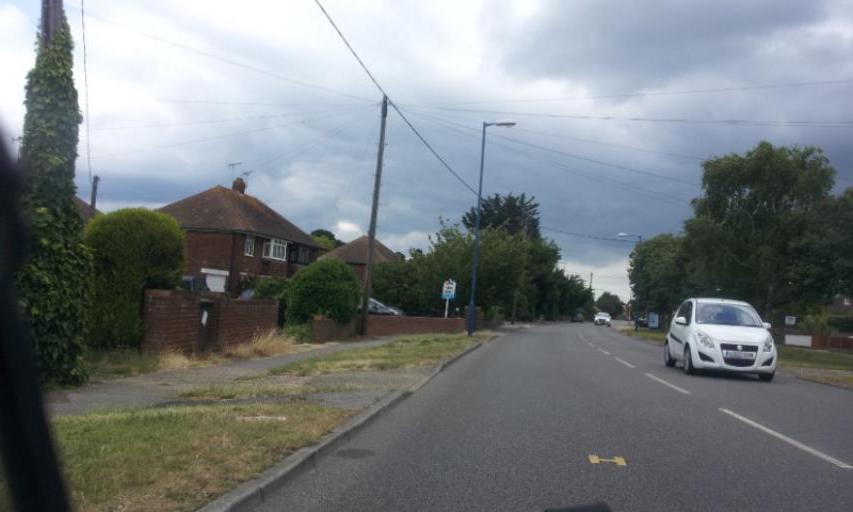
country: GB
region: England
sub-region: Kent
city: Tankerton
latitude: 51.3632
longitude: 1.0697
